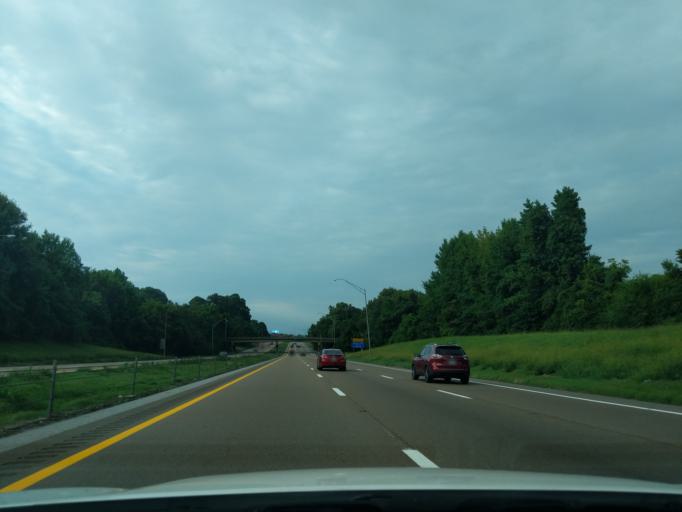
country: US
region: Tennessee
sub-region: Shelby County
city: New South Memphis
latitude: 35.0995
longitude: -90.0762
